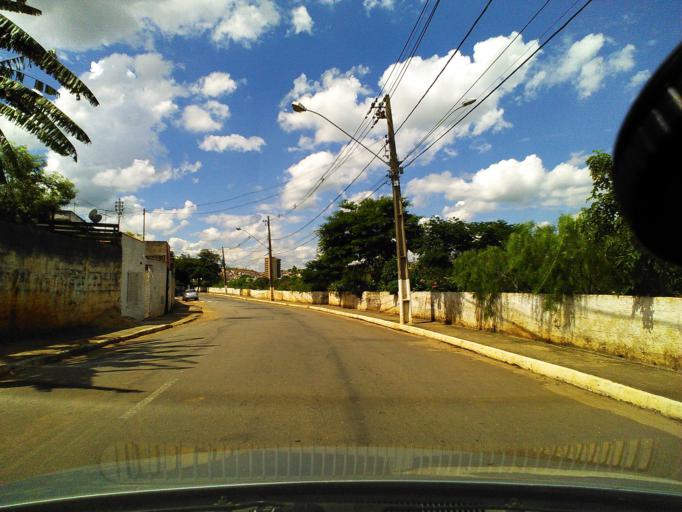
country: BR
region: Minas Gerais
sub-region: Tres Coracoes
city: Tres Coracoes
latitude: -21.7037
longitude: -45.2604
